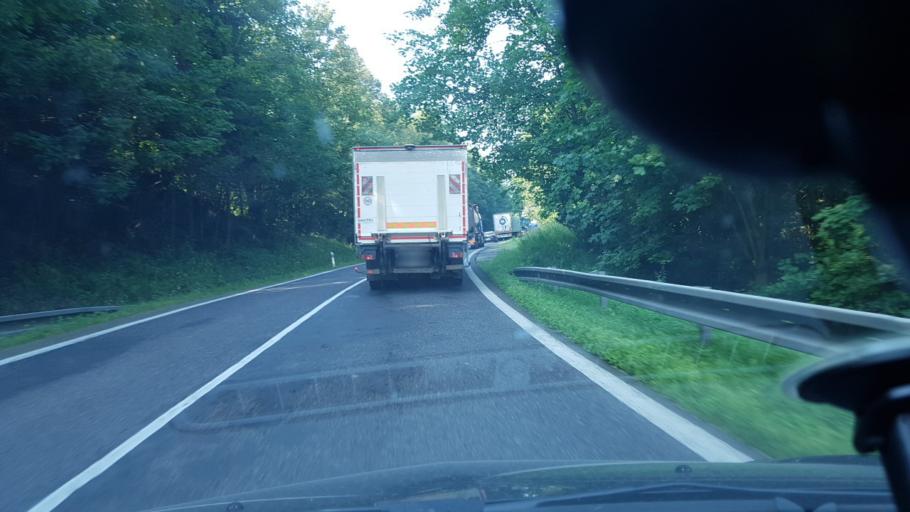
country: SK
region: Zilinsky
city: Tvrdosin
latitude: 49.2888
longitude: 19.4936
